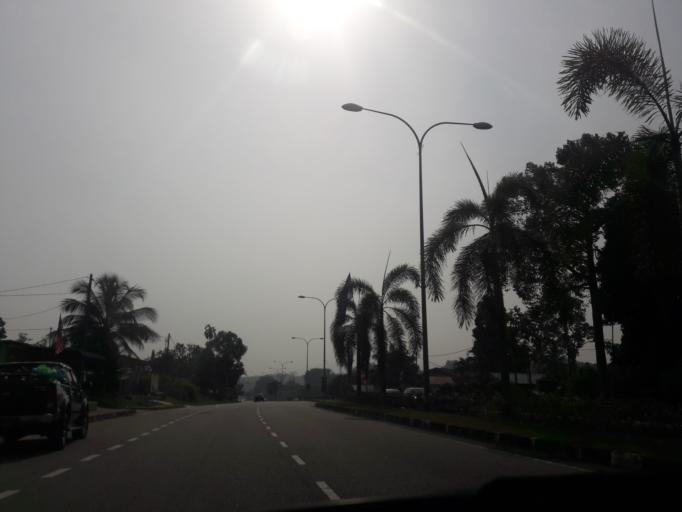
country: MY
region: Kedah
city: Kulim
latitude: 5.3540
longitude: 100.5348
